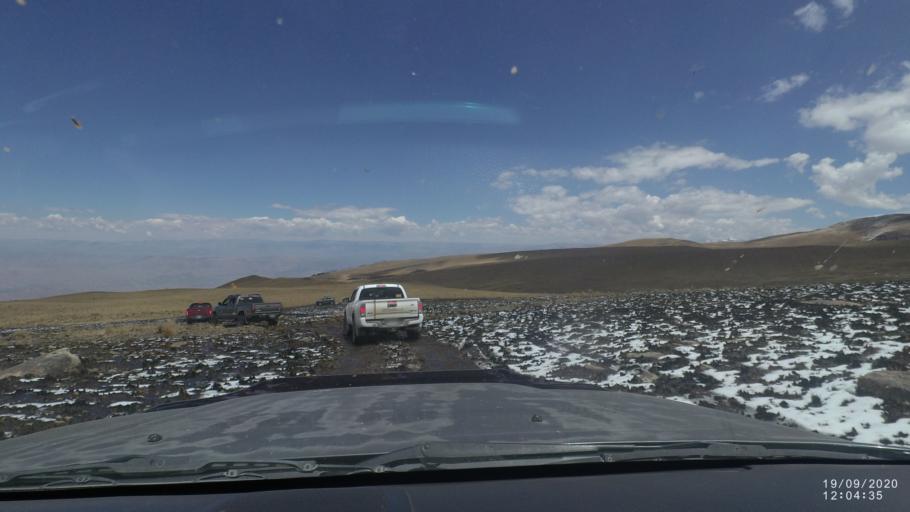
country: BO
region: Cochabamba
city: Cochabamba
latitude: -17.2996
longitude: -66.1073
